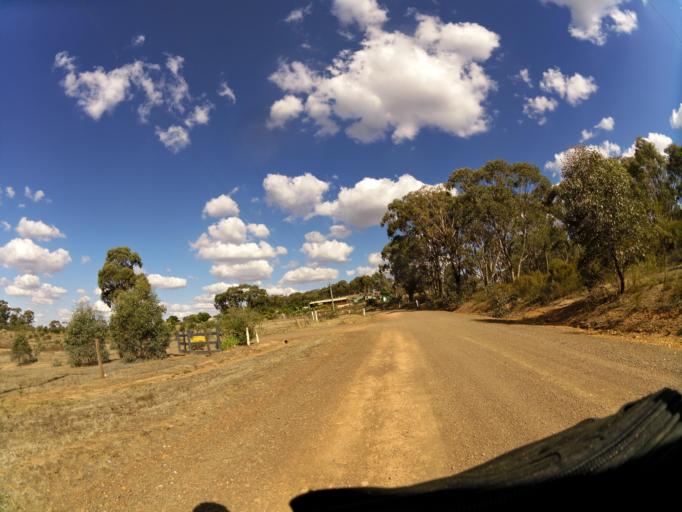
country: AU
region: Victoria
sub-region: Greater Bendigo
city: Kennington
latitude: -36.9546
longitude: 144.7768
